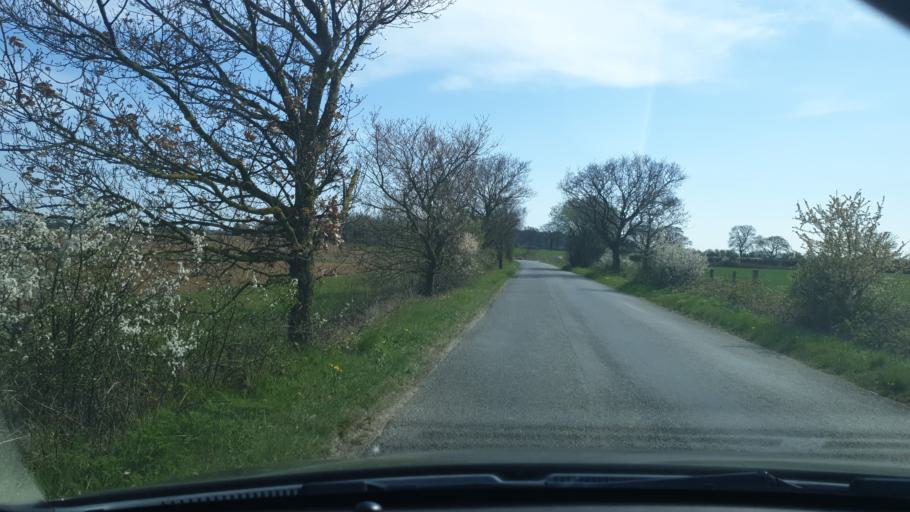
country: GB
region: England
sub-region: Essex
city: Great Bentley
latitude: 51.8506
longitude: 1.0867
